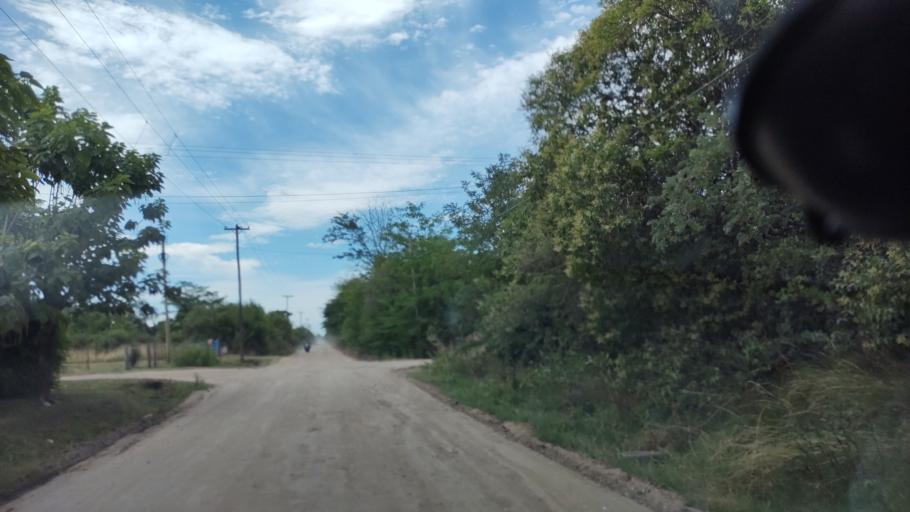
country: AR
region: Buenos Aires
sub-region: Partido de Lobos
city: Lobos
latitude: -35.1701
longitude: -59.1087
